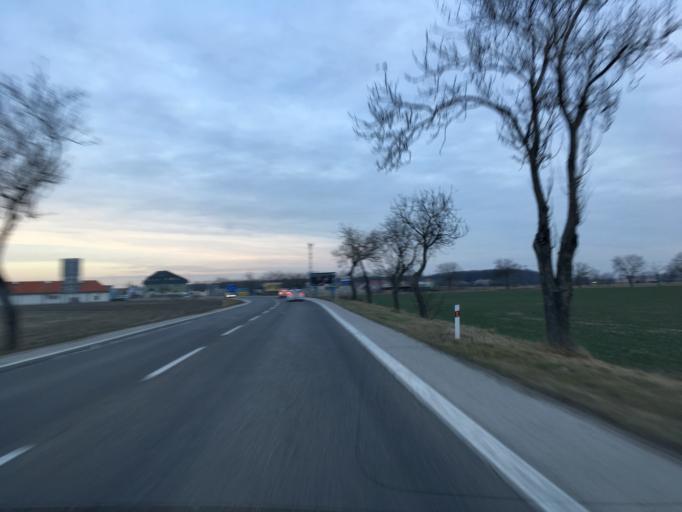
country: SK
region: Trnavsky
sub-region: Okres Dunajska Streda
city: Velky Meder
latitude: 47.8660
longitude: 17.7574
